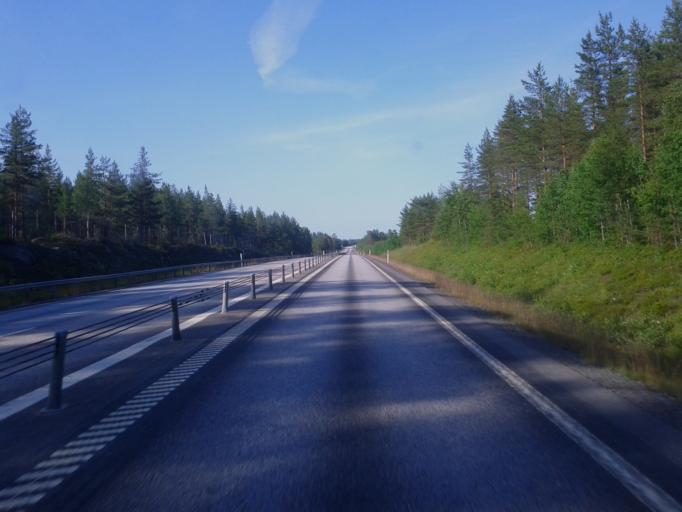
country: SE
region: Vaesterbotten
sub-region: Umea Kommun
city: Saevar
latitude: 63.9396
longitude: 20.6500
